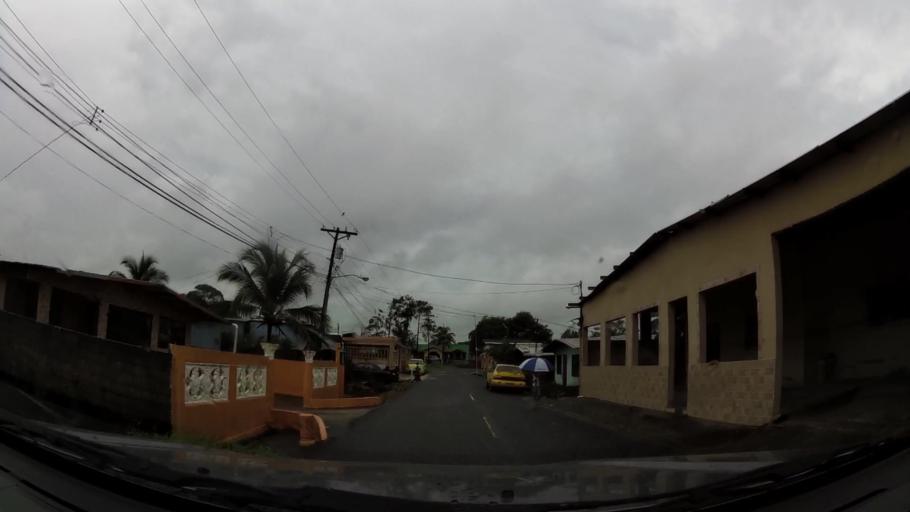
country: PA
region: Colon
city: Arco Iris
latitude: 9.3353
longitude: -79.8771
